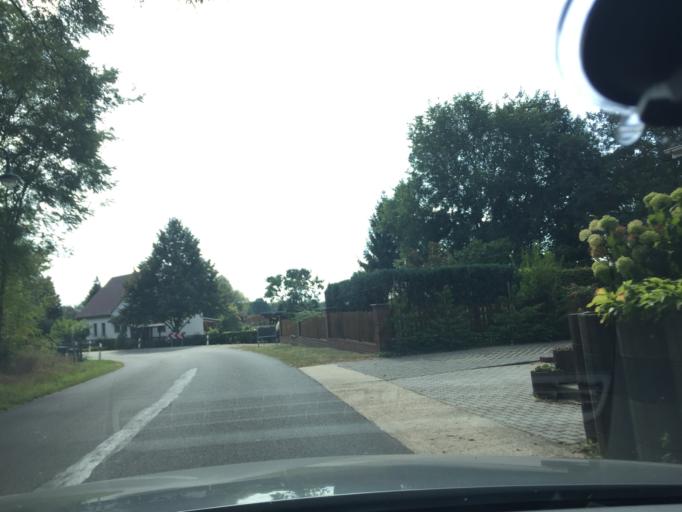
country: DE
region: Brandenburg
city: Grunheide
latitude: 52.3747
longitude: 13.7984
